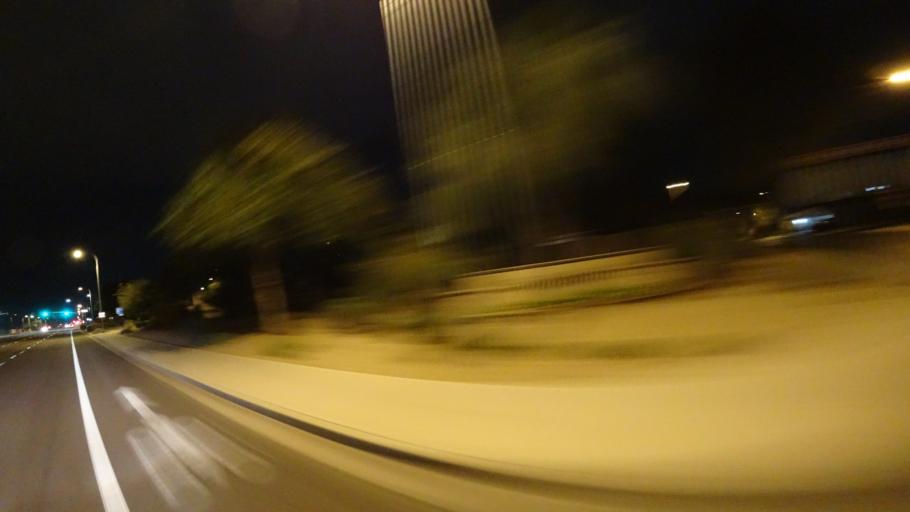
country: US
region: Arizona
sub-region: Maricopa County
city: Chandler
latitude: 33.2915
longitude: -111.8349
